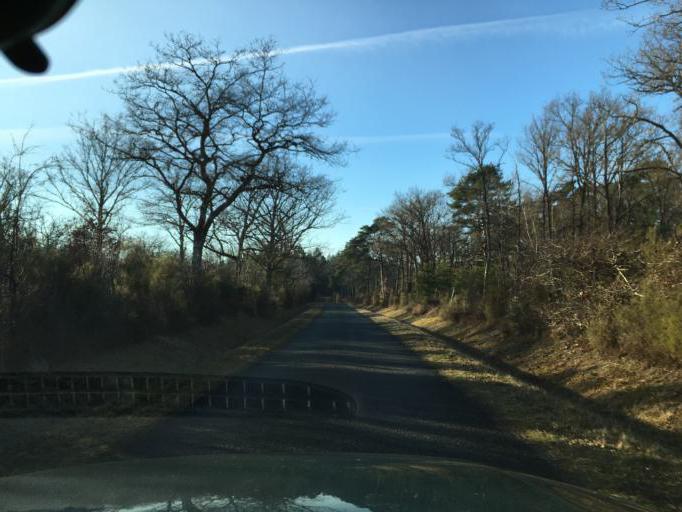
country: FR
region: Centre
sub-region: Departement du Loiret
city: Ligny-le-Ribault
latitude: 47.6934
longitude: 1.7602
